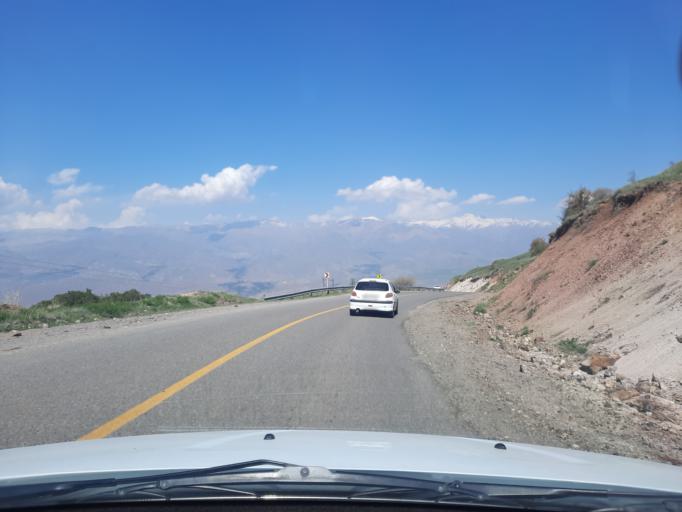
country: IR
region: Qazvin
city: Qazvin
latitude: 36.4128
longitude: 50.2373
